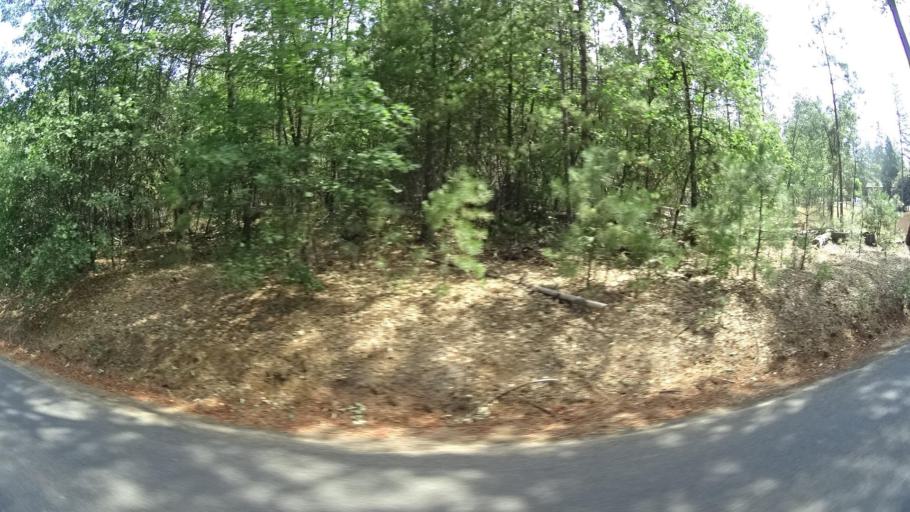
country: US
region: California
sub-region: Tuolumne County
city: Tuolumne City
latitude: 37.7596
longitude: -120.1431
